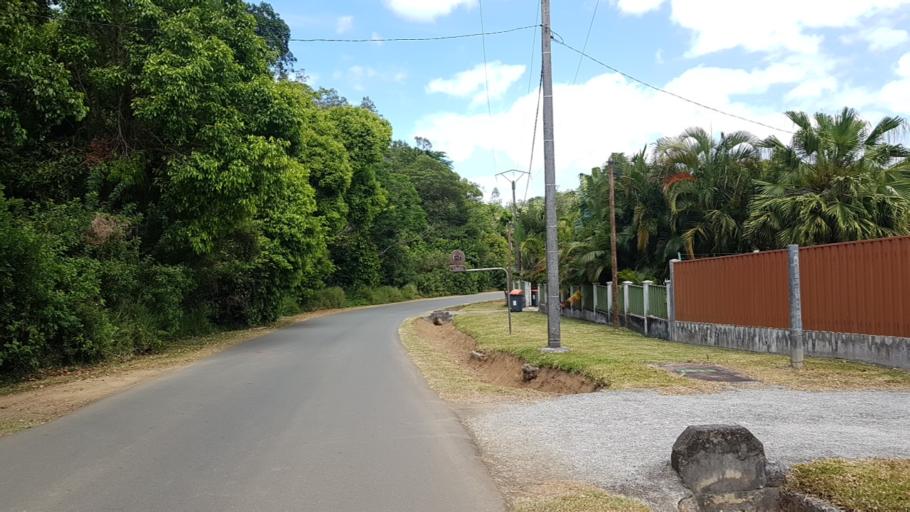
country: NC
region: South Province
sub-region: Dumbea
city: Dumbea
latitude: -22.1783
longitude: 166.4825
